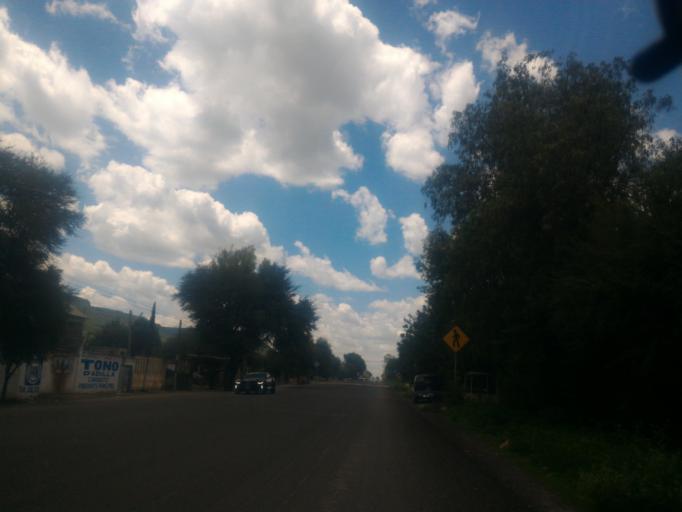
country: MX
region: Guanajuato
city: San Roque
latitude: 20.9601
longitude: -101.8977
